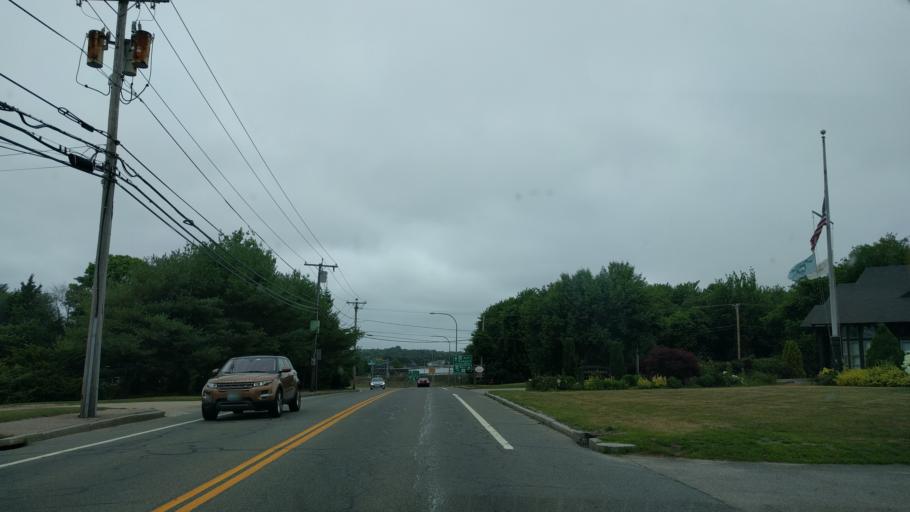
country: US
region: Rhode Island
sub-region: Newport County
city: Jamestown
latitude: 41.5066
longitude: -71.3647
